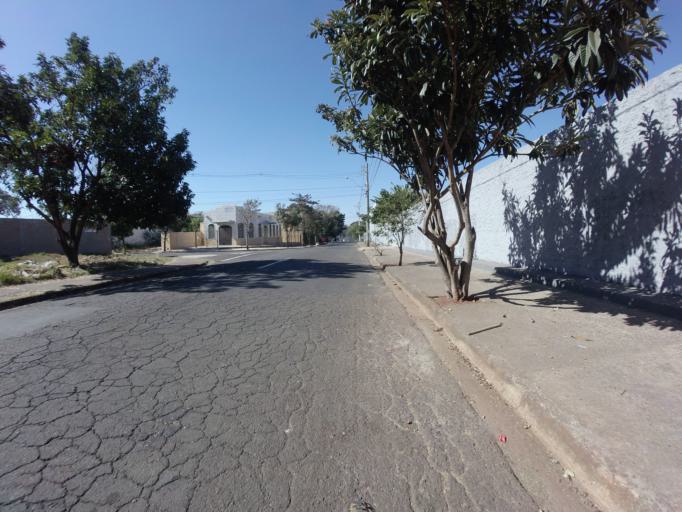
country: BR
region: Sao Paulo
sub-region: Piracicaba
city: Piracicaba
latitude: -22.7696
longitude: -47.5887
